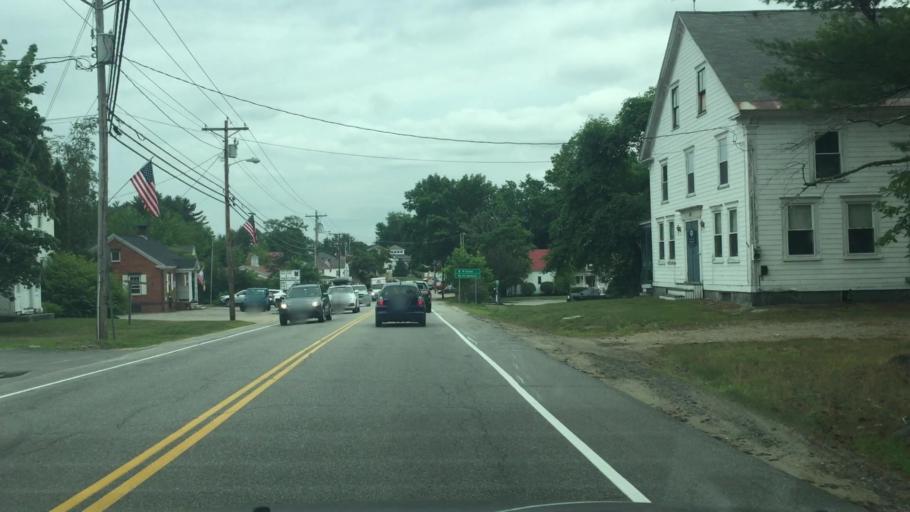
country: US
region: New Hampshire
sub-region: Carroll County
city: Moultonborough
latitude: 43.7534
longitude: -71.3981
